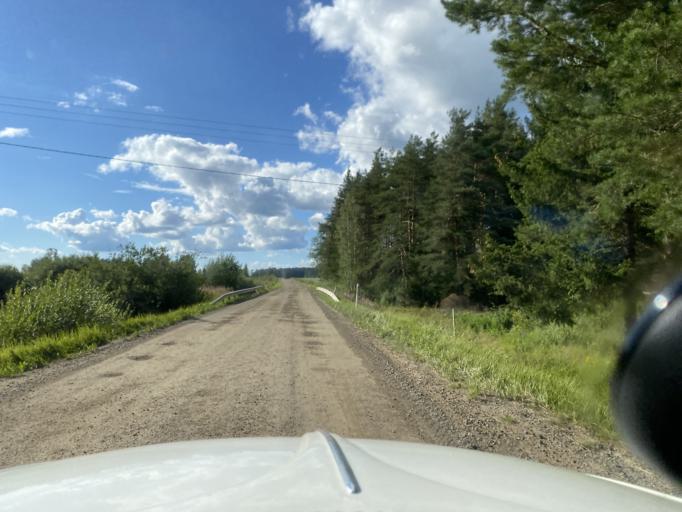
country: FI
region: Pirkanmaa
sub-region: Lounais-Pirkanmaa
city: Punkalaidun
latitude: 61.1315
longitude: 23.2370
